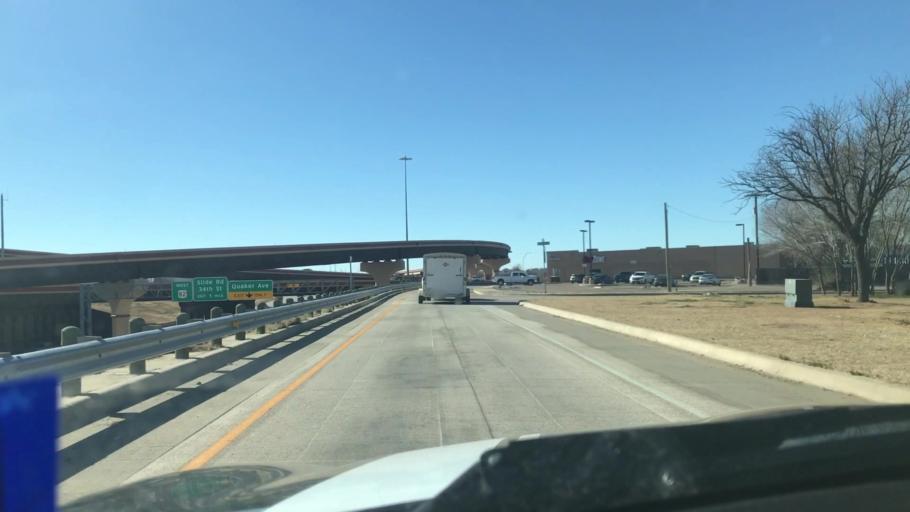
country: US
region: Texas
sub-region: Lubbock County
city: Lubbock
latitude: 33.5789
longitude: -101.8993
